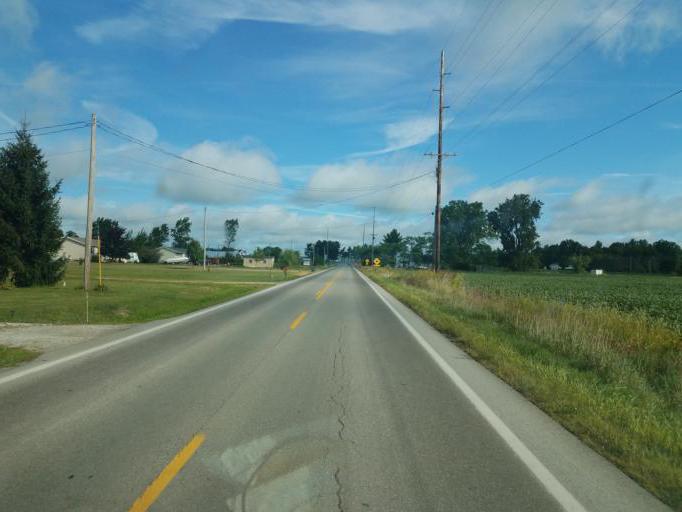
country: US
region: Ohio
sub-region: Wayne County
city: West Salem
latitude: 40.9889
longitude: -82.1100
